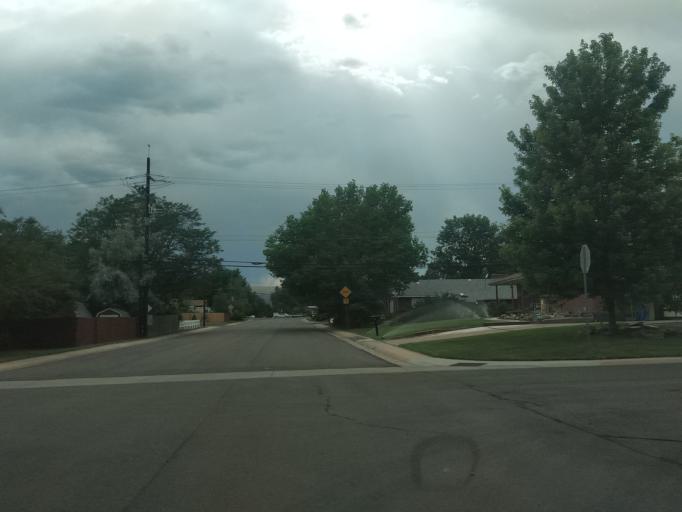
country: US
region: Colorado
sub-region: Jefferson County
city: Lakewood
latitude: 39.7002
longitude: -105.0978
